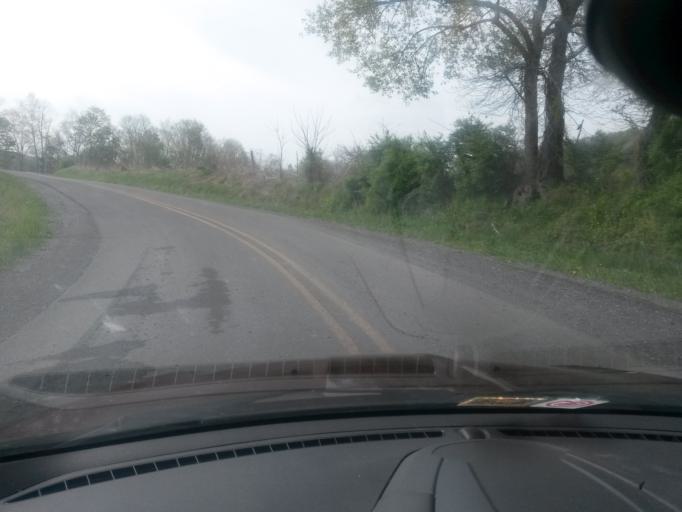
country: US
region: West Virginia
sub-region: Pocahontas County
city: Marlinton
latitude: 38.1040
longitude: -80.2263
